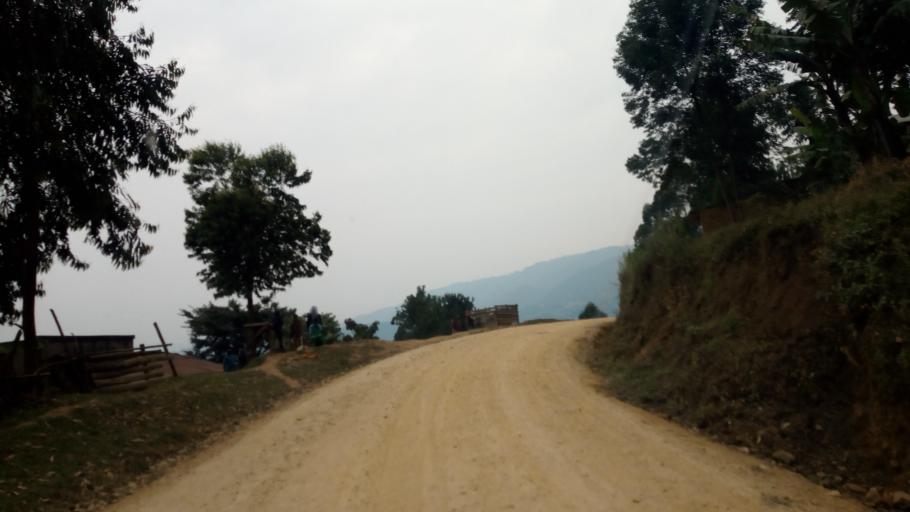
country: UG
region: Western Region
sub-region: Kanungu District
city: Kanungu
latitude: -1.1054
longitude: 29.8602
